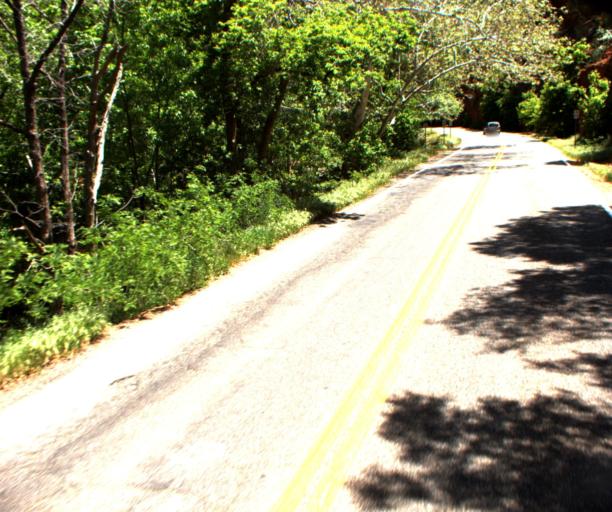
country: US
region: Arizona
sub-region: Coconino County
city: Sedona
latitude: 34.9295
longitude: -111.7401
